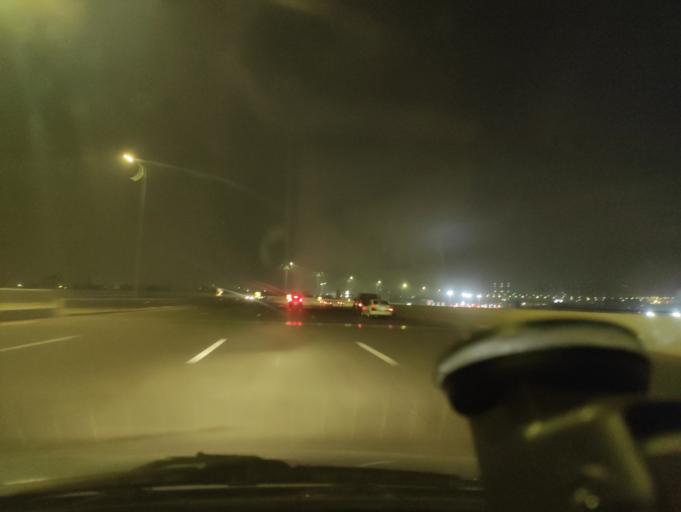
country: EG
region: Muhafazat al Qahirah
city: Cairo
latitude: 30.1125
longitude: 31.2197
